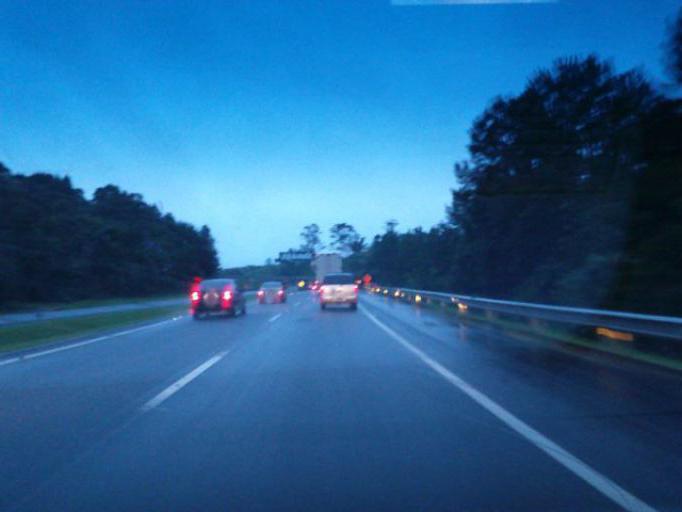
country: BR
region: Sao Paulo
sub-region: Juquitiba
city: Juquitiba
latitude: -23.9383
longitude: -47.0848
